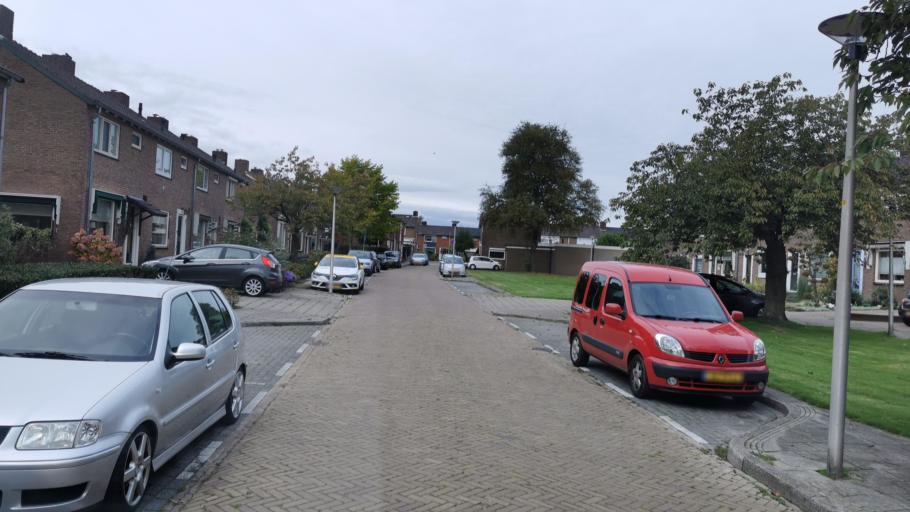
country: NL
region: Overijssel
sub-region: Gemeente Enschede
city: Enschede
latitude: 52.2071
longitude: 6.9094
